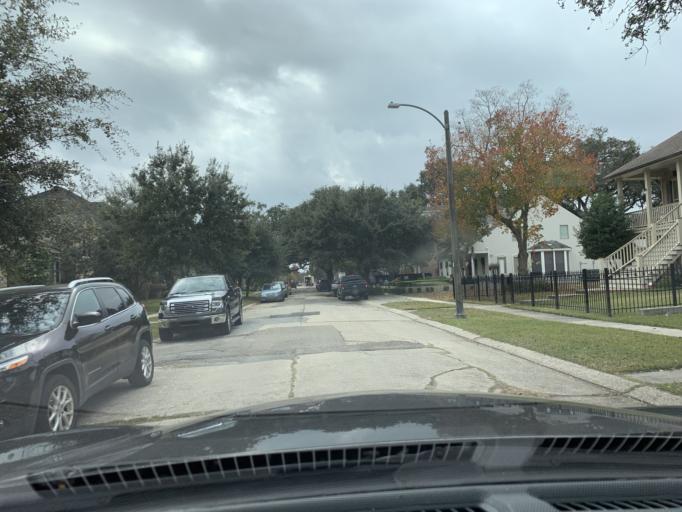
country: US
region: Louisiana
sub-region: Jefferson Parish
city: Metairie
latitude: 30.0152
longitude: -90.1035
